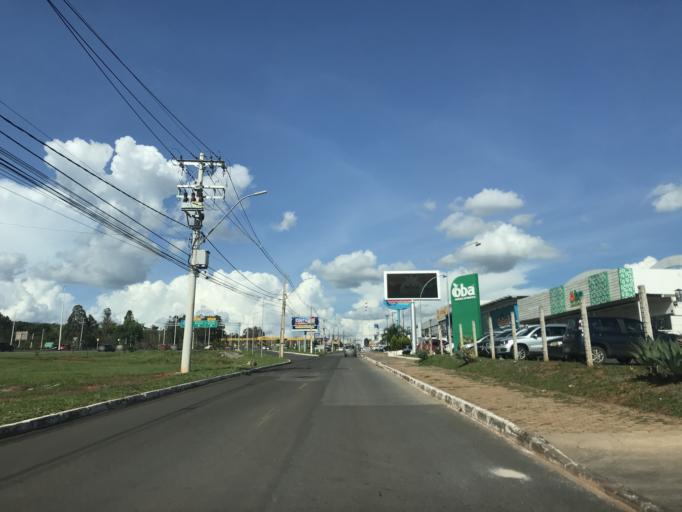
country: BR
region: Federal District
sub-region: Brasilia
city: Brasilia
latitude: -15.6961
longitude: -47.8740
